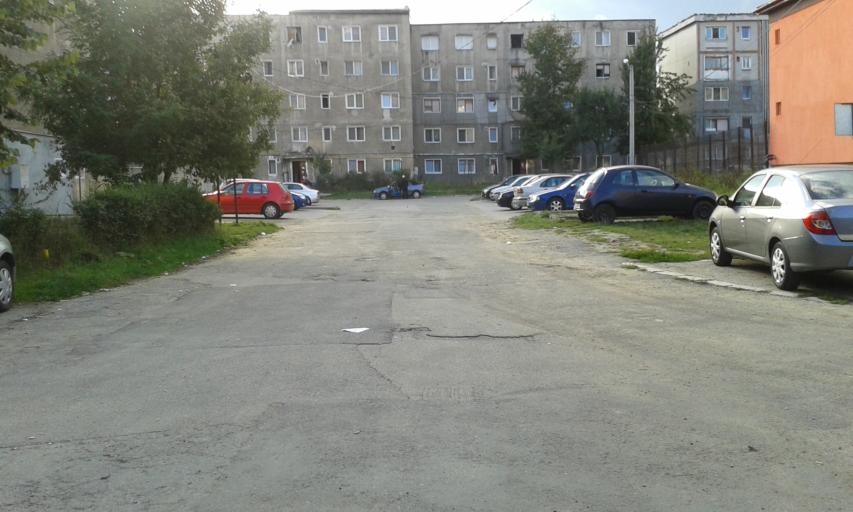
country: RO
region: Hunedoara
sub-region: Municipiul Petrosani
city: Petrosani
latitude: 45.3931
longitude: 23.3750
